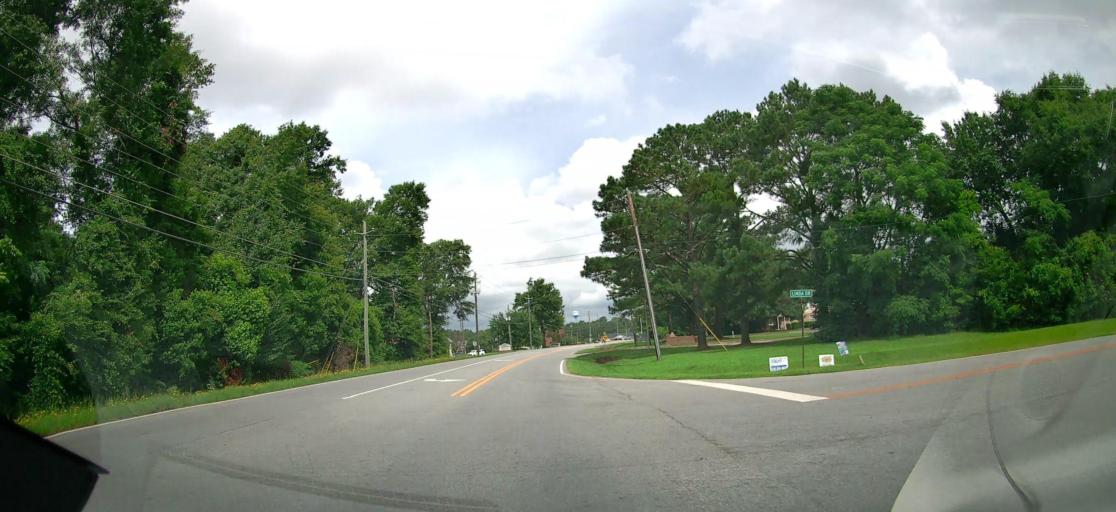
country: US
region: Georgia
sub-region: Peach County
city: Byron
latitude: 32.6476
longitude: -83.7551
